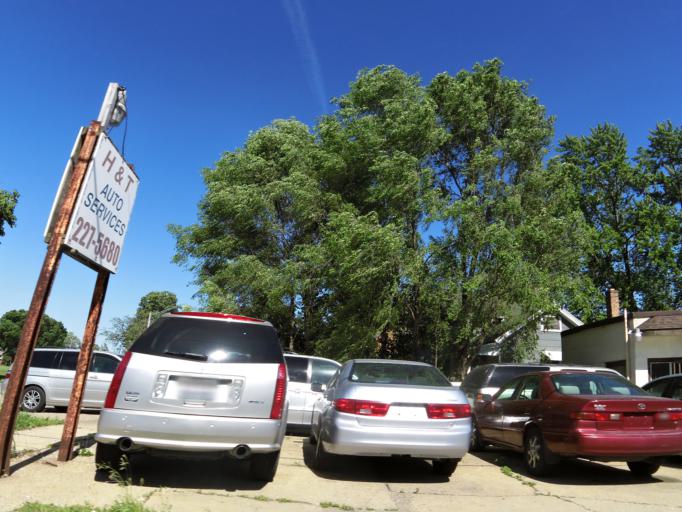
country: US
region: Illinois
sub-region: Winnebago County
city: Rockford
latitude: 42.2488
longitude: -89.0721
